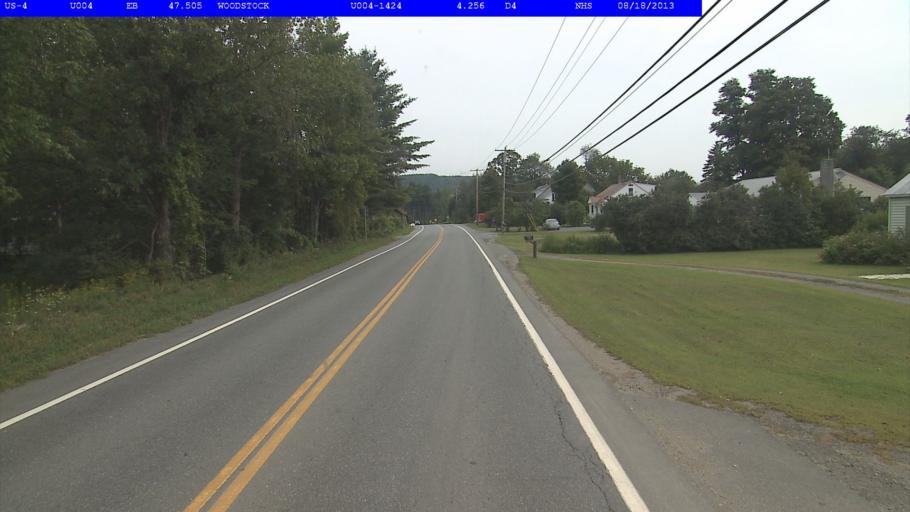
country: US
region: Vermont
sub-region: Windsor County
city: Woodstock
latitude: 43.6100
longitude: -72.5502
